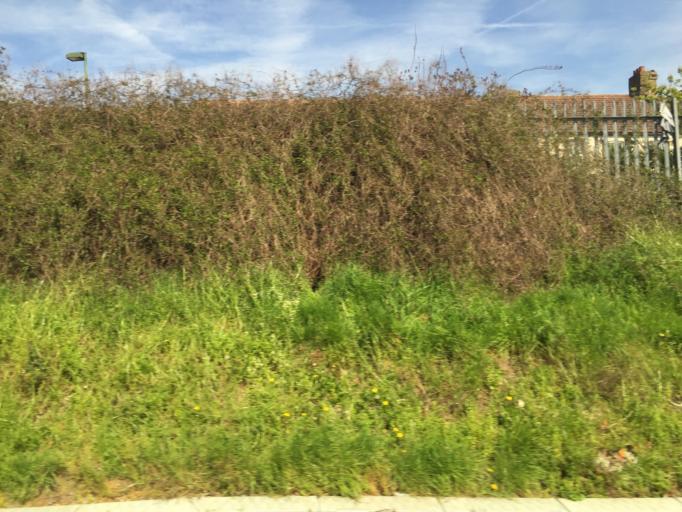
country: GB
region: England
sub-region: Greater London
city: Becontree
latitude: 51.5651
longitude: 0.1079
